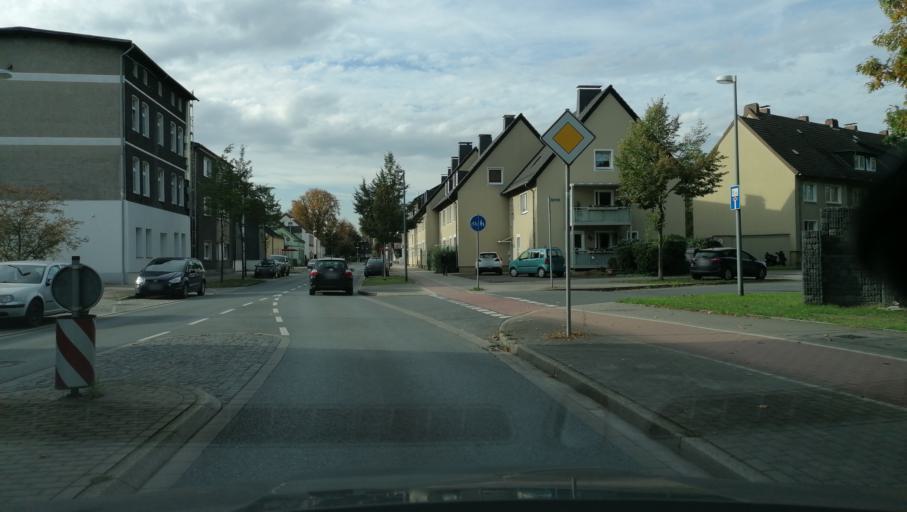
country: DE
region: North Rhine-Westphalia
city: Herten
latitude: 51.5817
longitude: 7.1544
